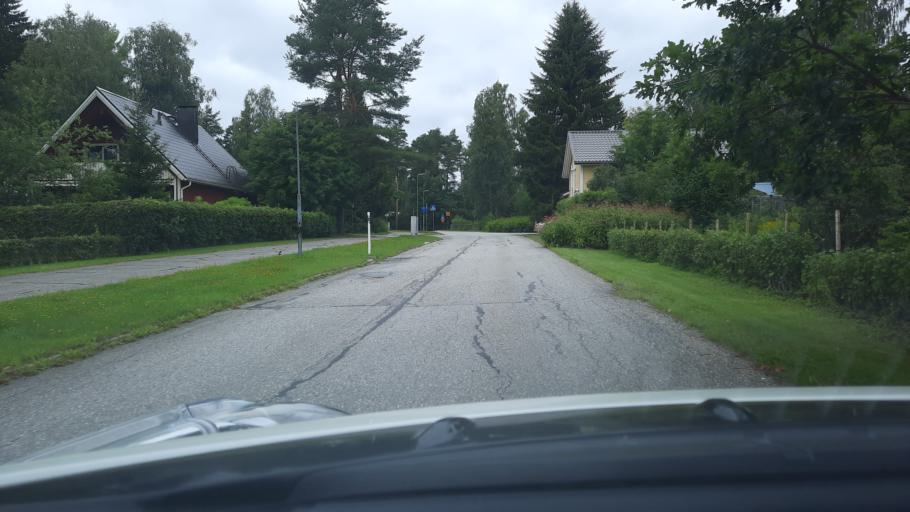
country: FI
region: North Karelia
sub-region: Joensuu
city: Joensuu
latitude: 62.6126
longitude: 29.8337
